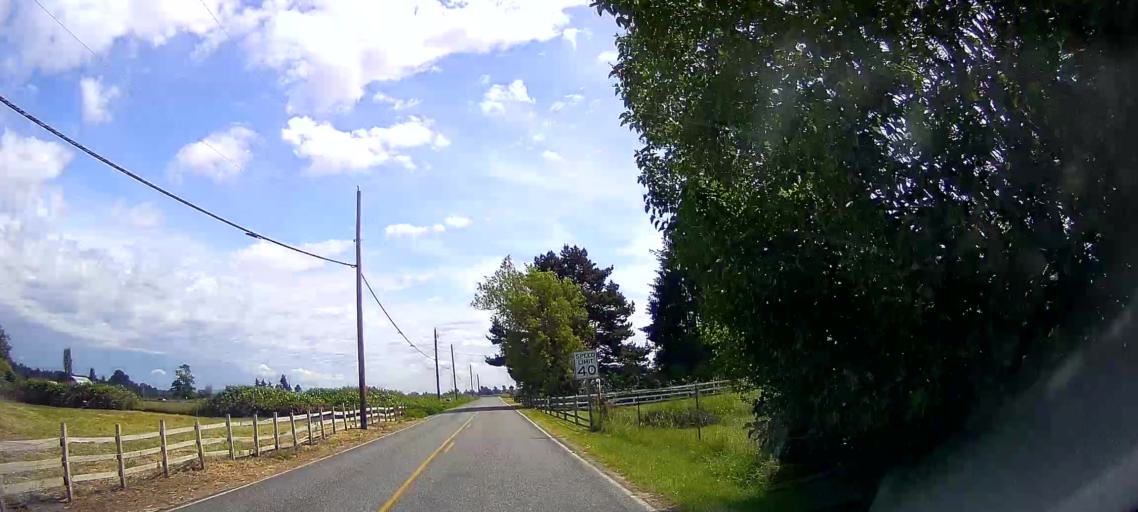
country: US
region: Washington
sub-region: Skagit County
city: Burlington
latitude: 48.5877
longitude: -122.4164
